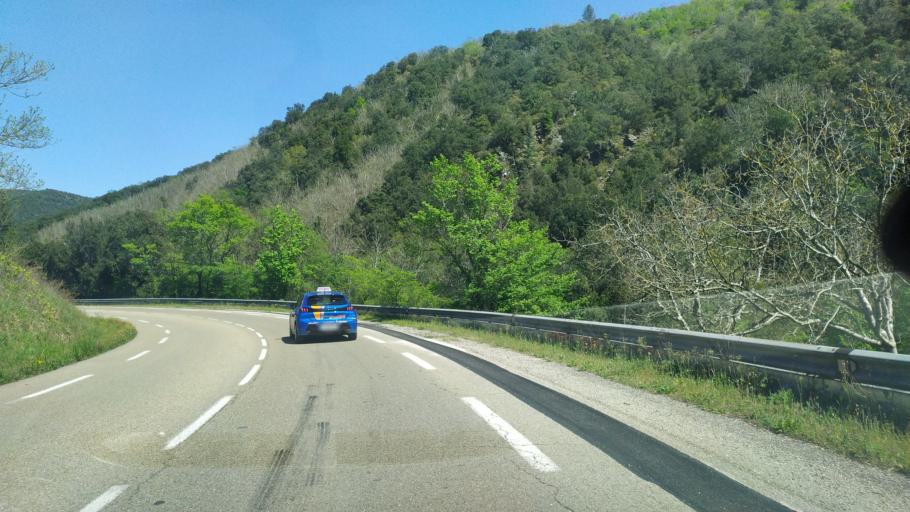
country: FR
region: Languedoc-Roussillon
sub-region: Departement du Gard
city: Le Vigan
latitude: 43.9970
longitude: 3.6456
